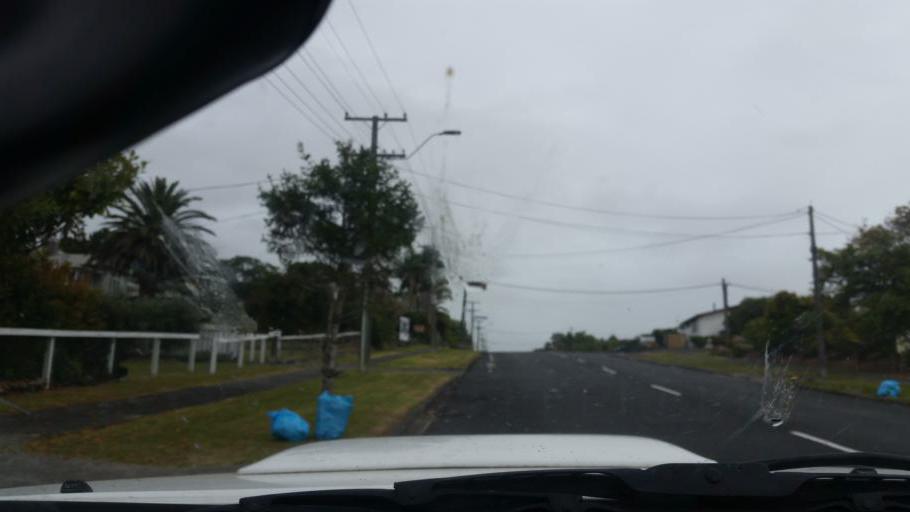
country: NZ
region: Northland
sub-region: Kaipara District
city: Dargaville
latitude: -35.9361
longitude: 173.8661
